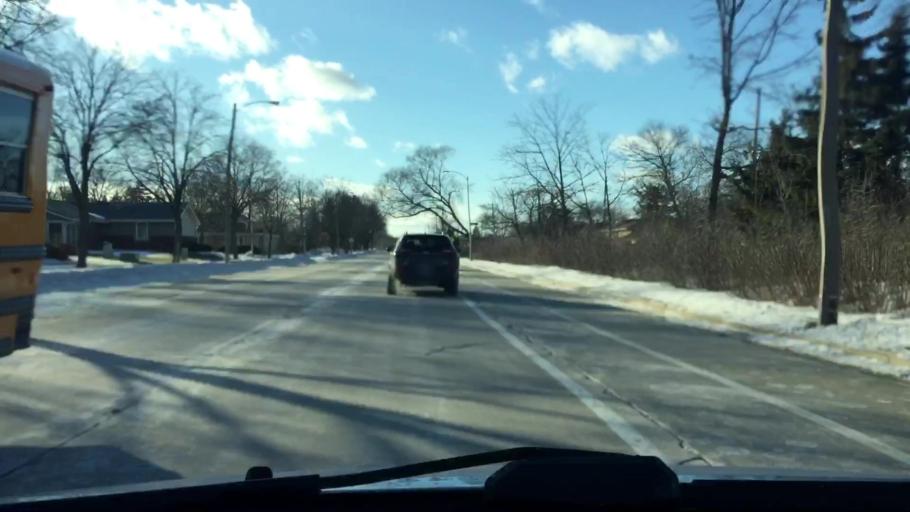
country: US
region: Wisconsin
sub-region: Milwaukee County
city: Greenfield
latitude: 42.9738
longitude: -88.0025
